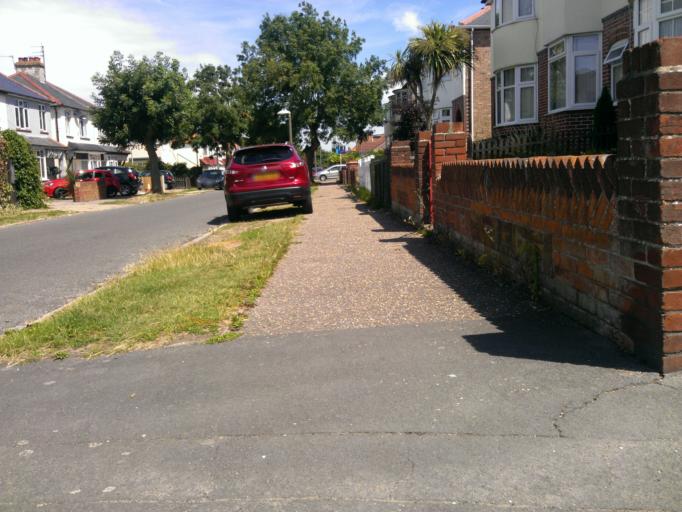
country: GB
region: England
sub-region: Essex
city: Clacton-on-Sea
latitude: 51.7997
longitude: 1.1534
